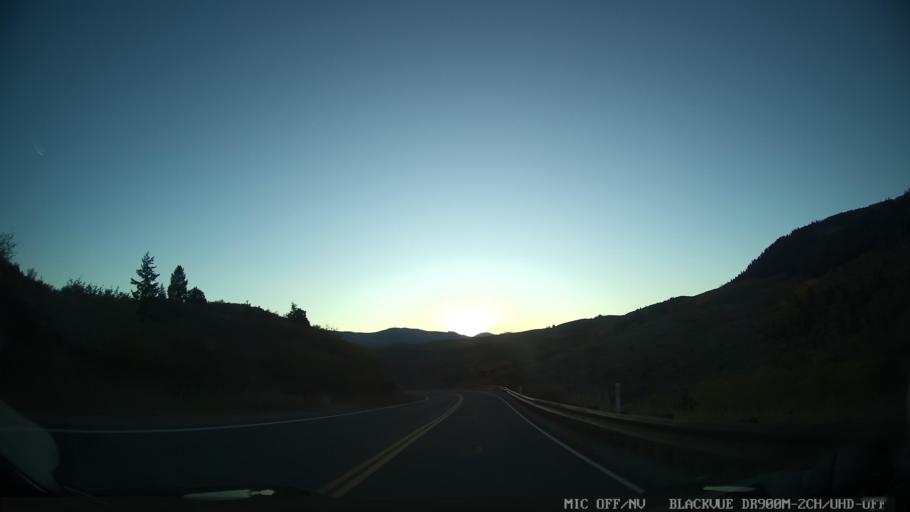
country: US
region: Colorado
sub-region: Eagle County
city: Edwards
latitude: 39.8151
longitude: -106.6658
